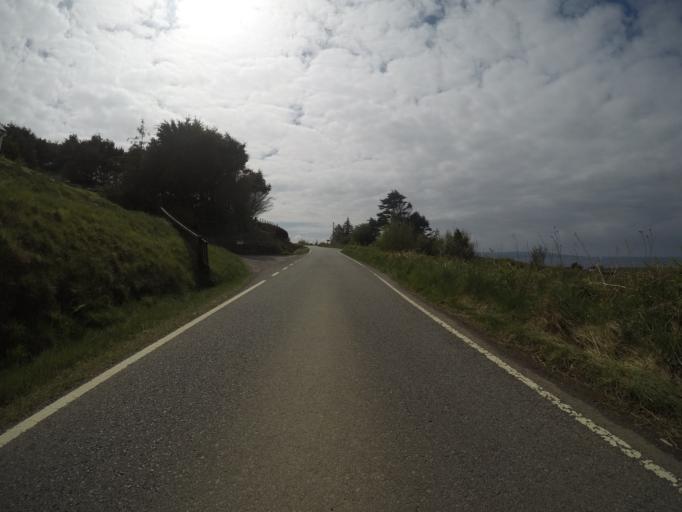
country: GB
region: Scotland
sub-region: Highland
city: Portree
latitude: 57.6119
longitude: -6.3719
